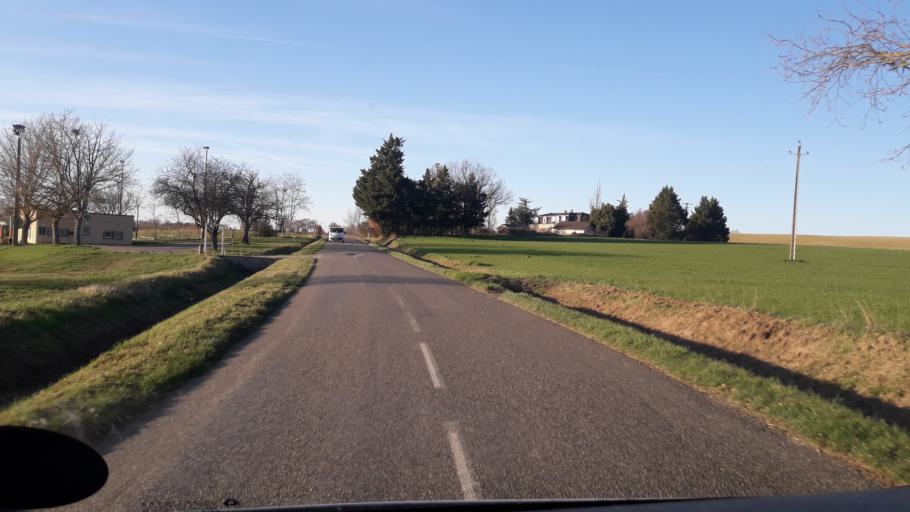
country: FR
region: Midi-Pyrenees
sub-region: Departement du Gers
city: Gimont
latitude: 43.6049
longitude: 0.9791
